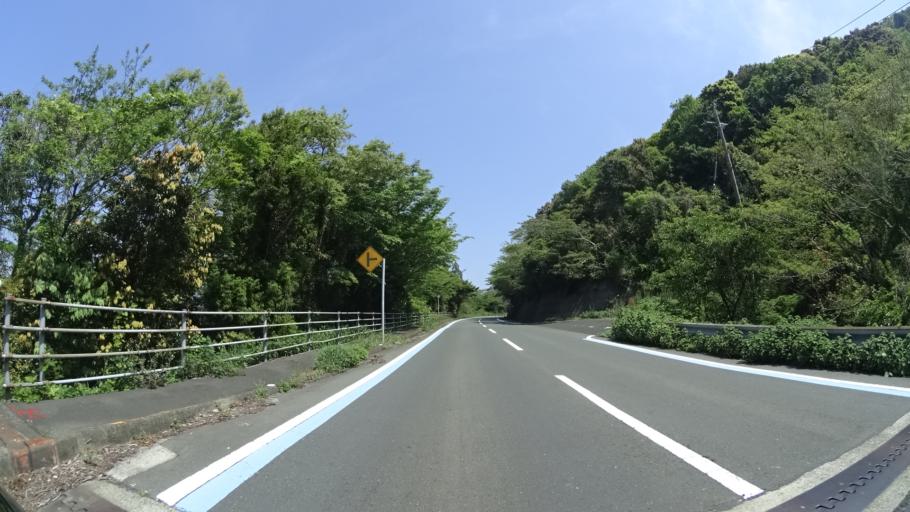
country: JP
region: Ehime
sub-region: Nishiuwa-gun
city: Ikata-cho
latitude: 33.4131
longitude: 132.1724
